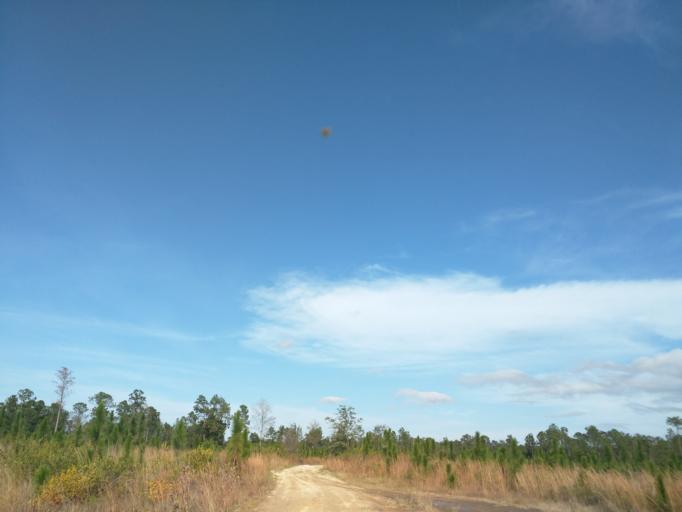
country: US
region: Florida
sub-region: Escambia County
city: Cantonment
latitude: 30.5469
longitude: -87.4306
